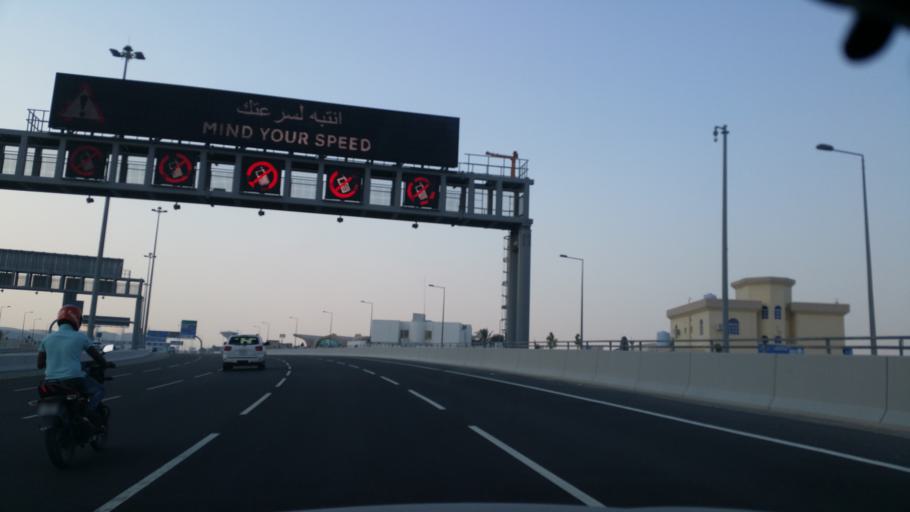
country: QA
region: Baladiyat ar Rayyan
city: Ar Rayyan
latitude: 25.3072
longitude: 51.4554
